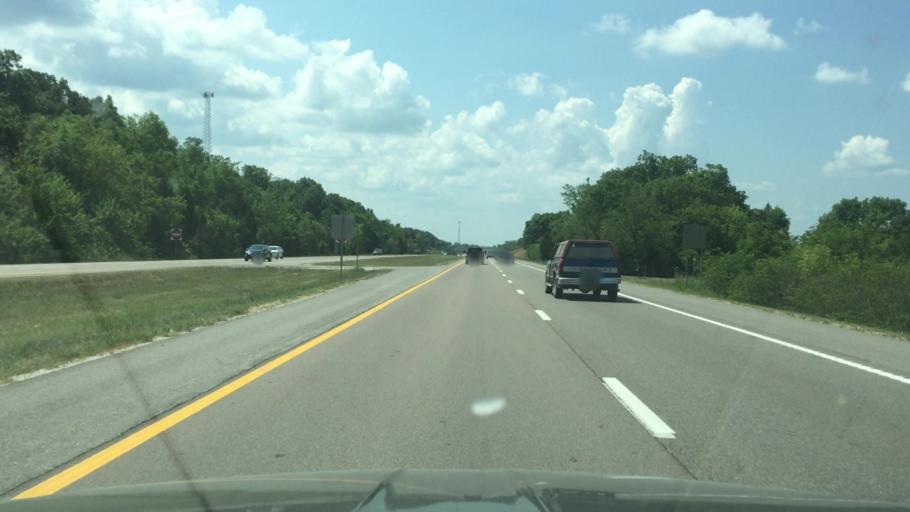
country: US
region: Missouri
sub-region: Miller County
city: Eldon
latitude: 38.2847
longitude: -92.5811
